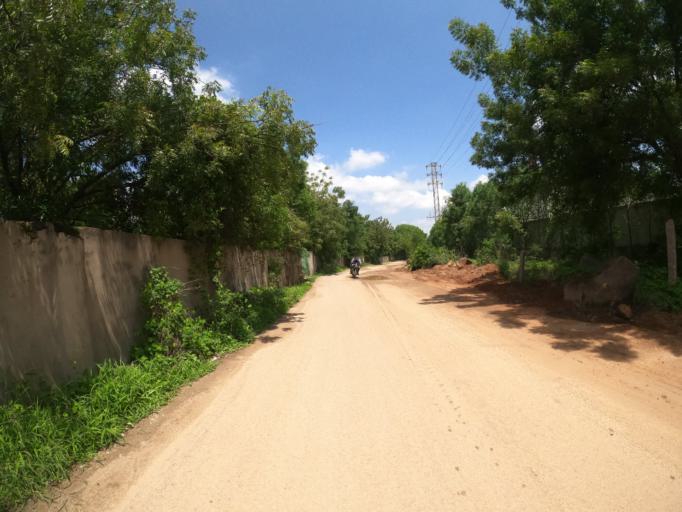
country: IN
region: Telangana
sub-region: Medak
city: Serilingampalle
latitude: 17.3739
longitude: 78.3239
